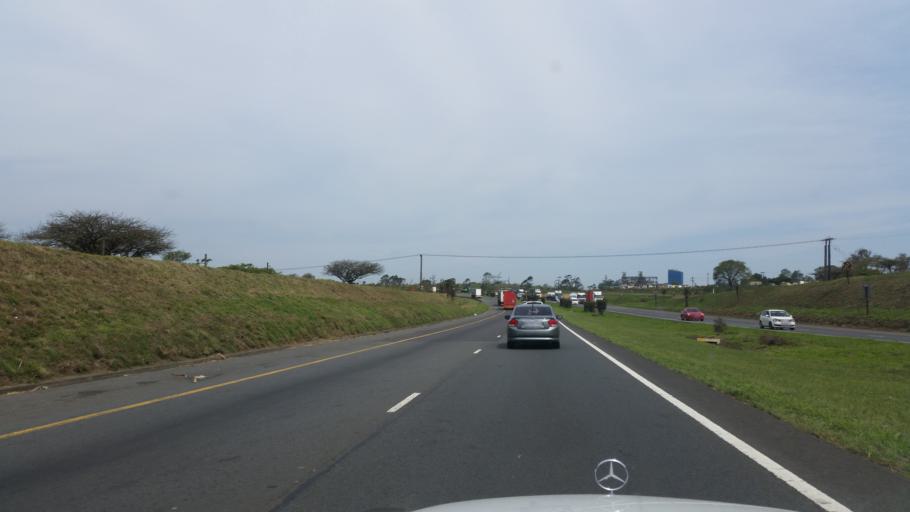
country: ZA
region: KwaZulu-Natal
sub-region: uMgungundlovu District Municipality
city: Camperdown
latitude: -29.7219
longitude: 30.5006
